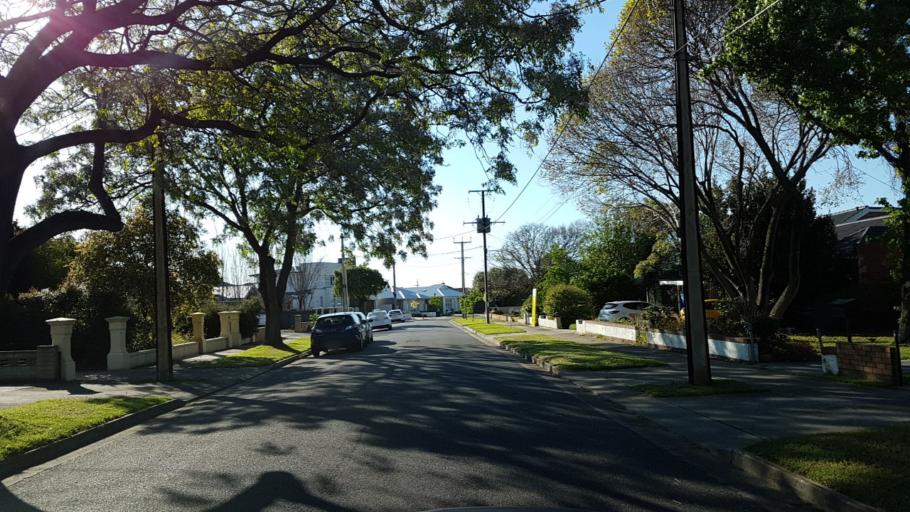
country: AU
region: South Australia
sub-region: Charles Sturt
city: Seaton
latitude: -34.9228
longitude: 138.5188
